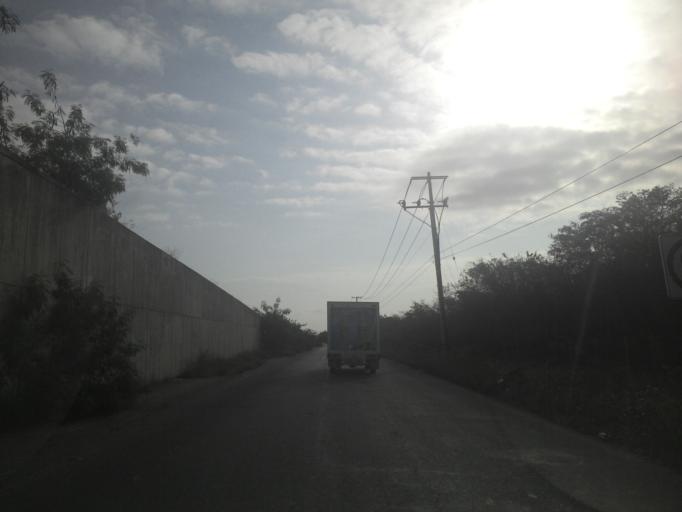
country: MX
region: Yucatan
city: Valladolid
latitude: 20.7250
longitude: -88.2022
